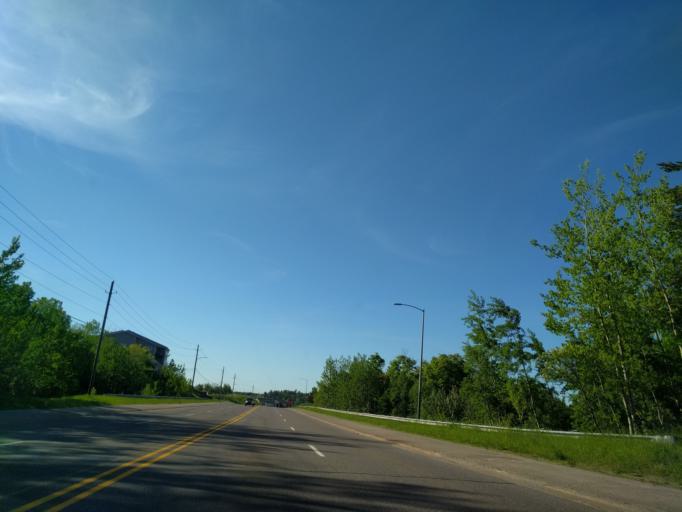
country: US
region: Michigan
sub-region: Marquette County
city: Marquette
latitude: 46.5393
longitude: -87.4177
